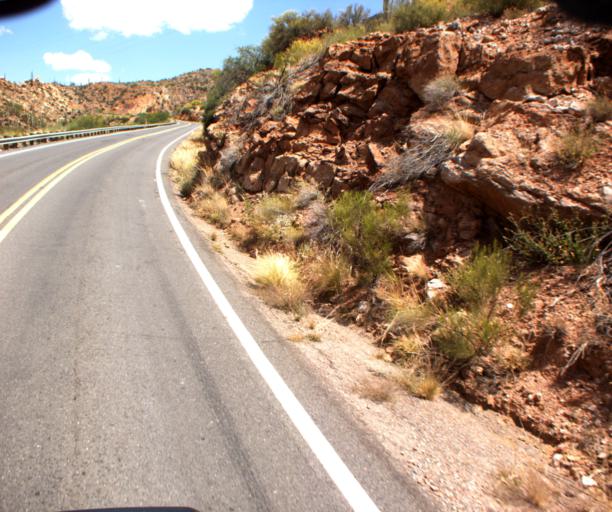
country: US
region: Arizona
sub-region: Pinal County
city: Superior
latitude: 33.1957
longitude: -111.0541
